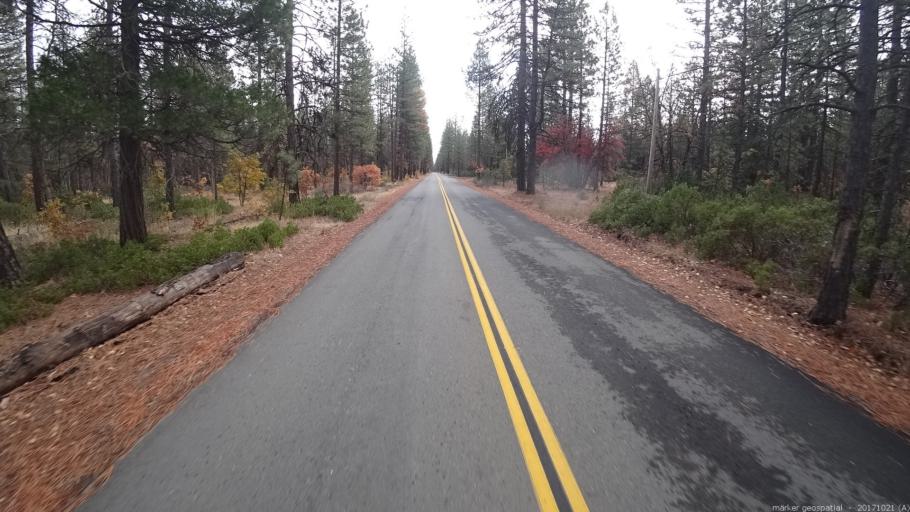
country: US
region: California
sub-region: Shasta County
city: Burney
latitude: 41.0056
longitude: -121.6468
